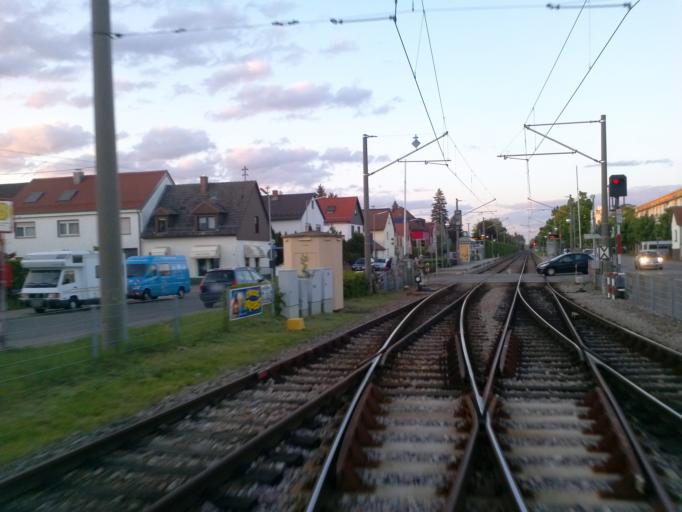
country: DE
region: Baden-Wuerttemberg
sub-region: Karlsruhe Region
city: Karlsruhe
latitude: 49.0442
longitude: 8.3733
